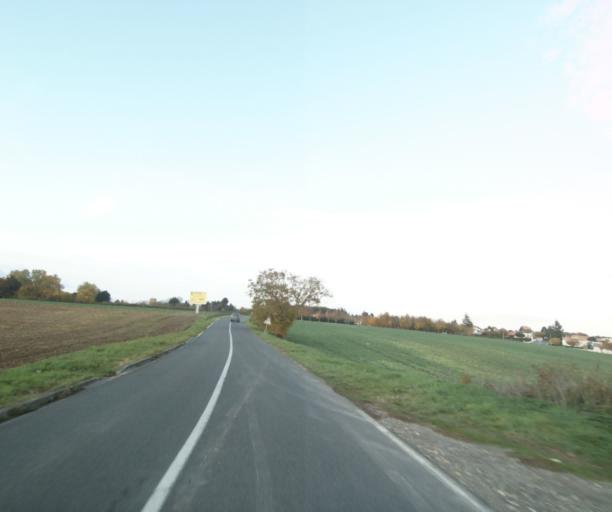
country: FR
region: Poitou-Charentes
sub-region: Departement de la Charente-Maritime
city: Saintes
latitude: 45.7575
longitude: -0.6387
